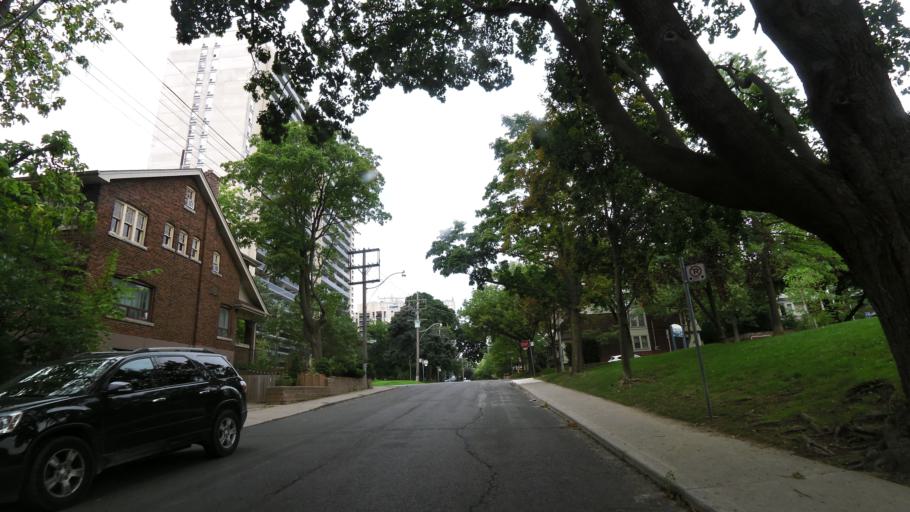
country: CA
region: Ontario
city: Toronto
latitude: 43.6581
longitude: -79.4632
